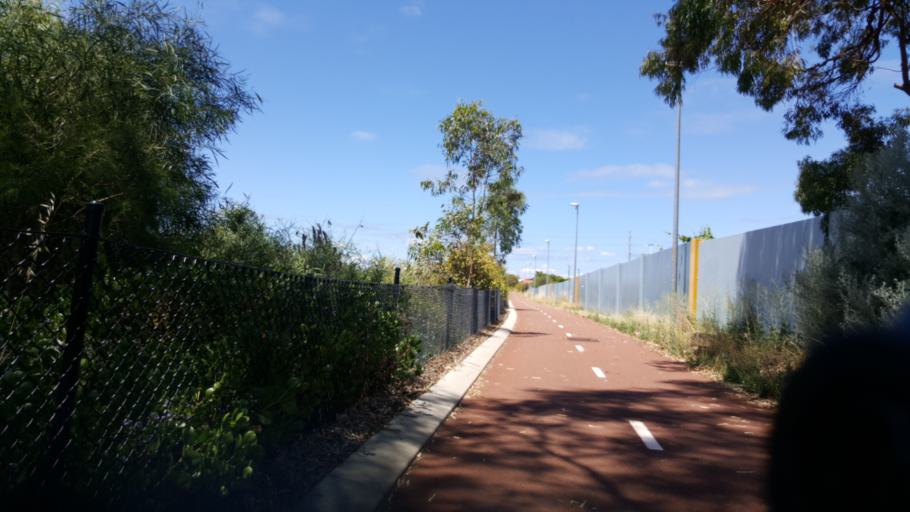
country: AU
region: Western Australia
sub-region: Bayswater
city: Embleton
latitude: -31.8688
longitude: 115.8864
